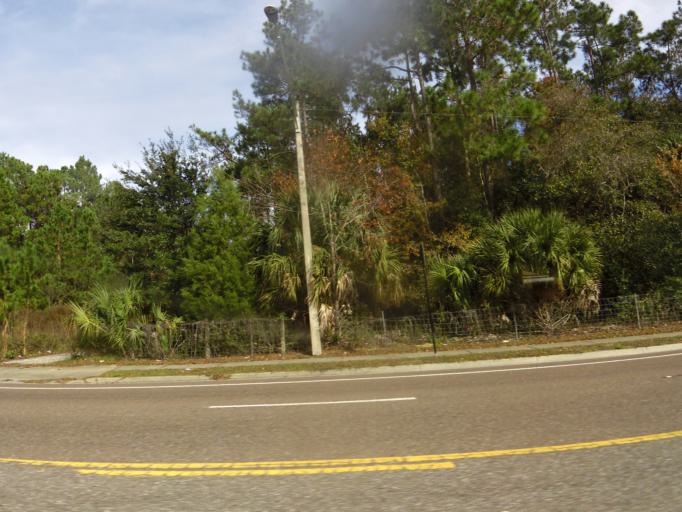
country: US
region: Florida
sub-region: Duval County
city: Jacksonville
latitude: 30.2515
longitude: -81.6147
